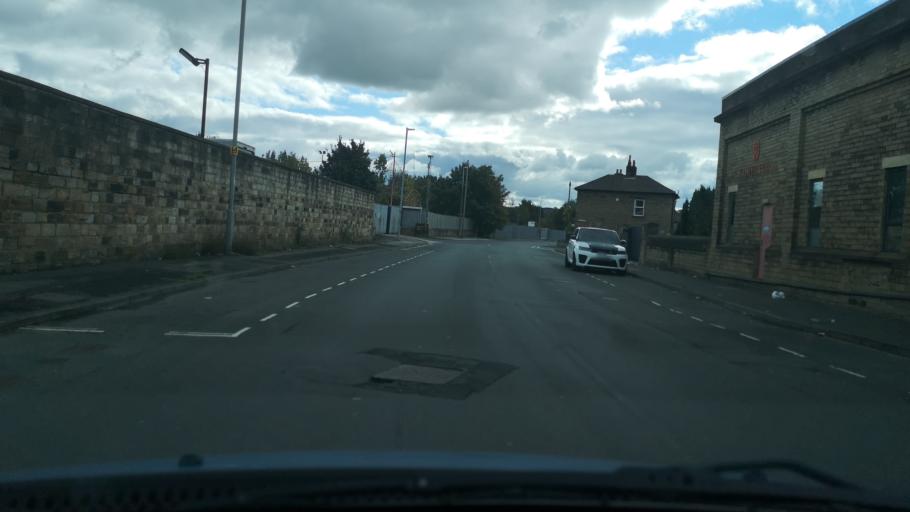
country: GB
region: England
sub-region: Kirklees
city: Dewsbury
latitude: 53.6851
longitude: -1.6233
